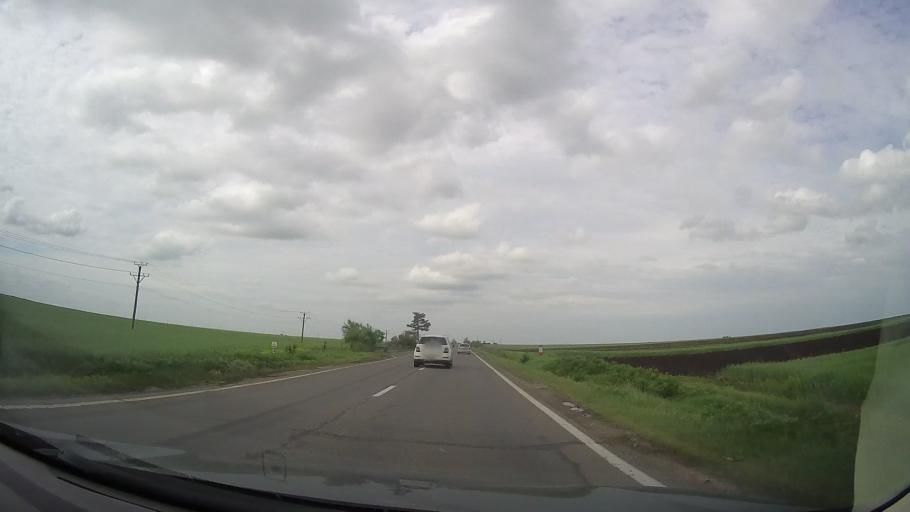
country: RO
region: Teleorman
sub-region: Comuna Rasmiresti
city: Rasmiresti
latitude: 44.0622
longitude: 25.5230
